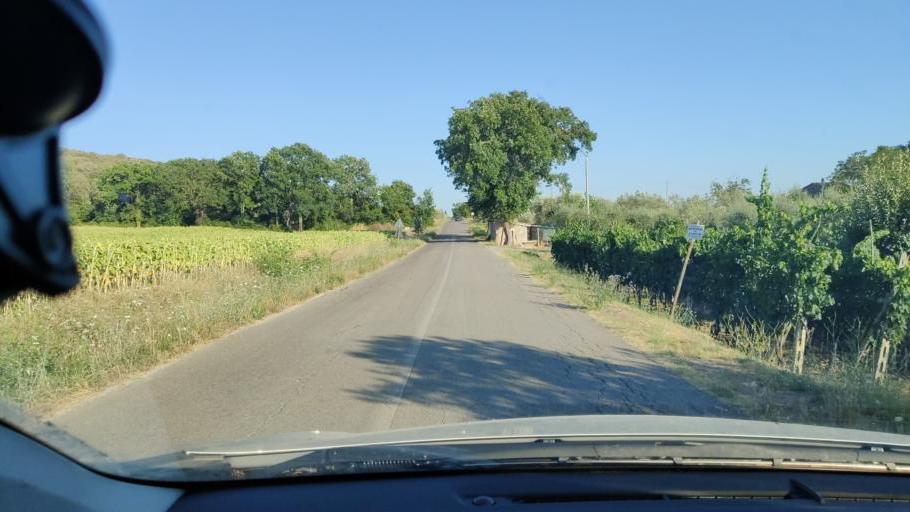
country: IT
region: Umbria
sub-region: Provincia di Terni
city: Lugnano in Teverina
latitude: 42.5474
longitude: 12.3499
